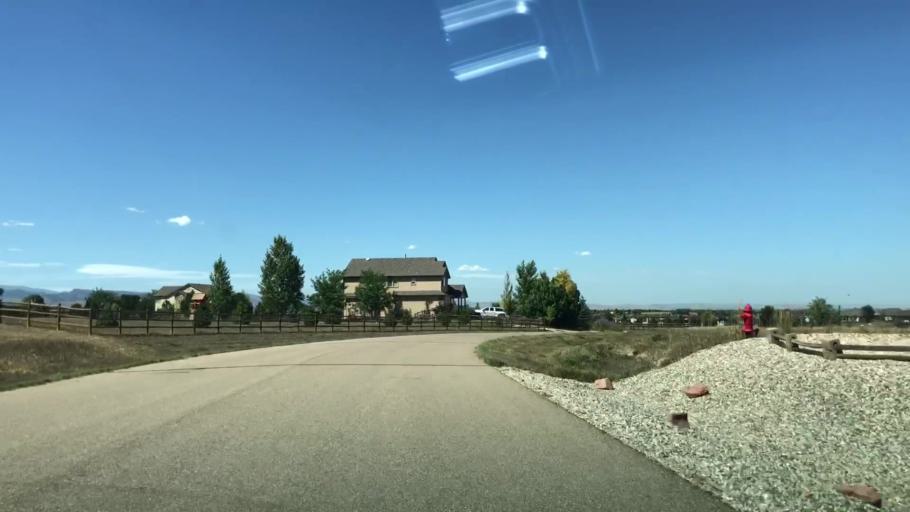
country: US
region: Colorado
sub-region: Weld County
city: Windsor
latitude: 40.4460
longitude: -104.9584
